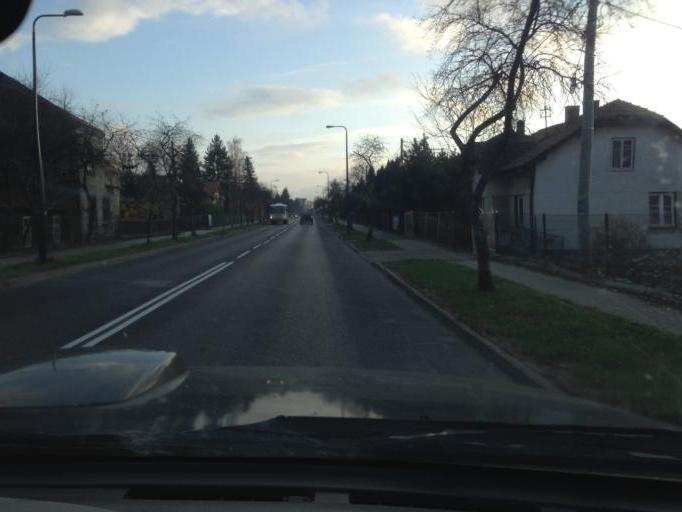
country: PL
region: Subcarpathian Voivodeship
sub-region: Powiat jasielski
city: Jaslo
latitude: 49.7581
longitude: 21.4716
